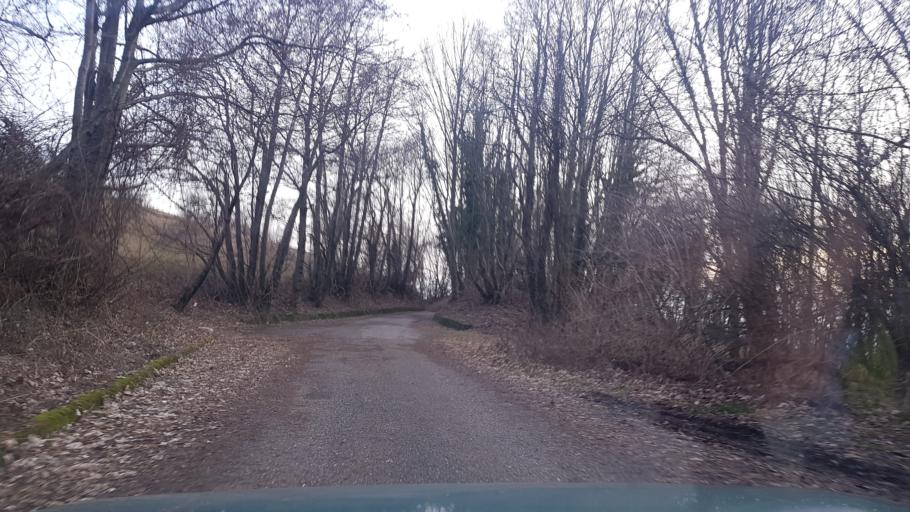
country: IT
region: Friuli Venezia Giulia
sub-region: Provincia di Udine
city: Pulfero
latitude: 46.1508
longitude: 13.4576
